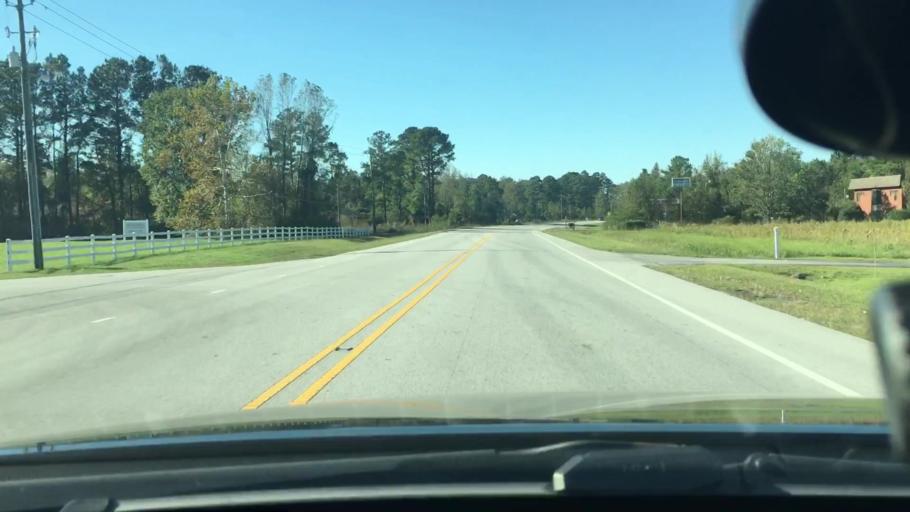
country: US
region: North Carolina
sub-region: Craven County
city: Trent Woods
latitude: 35.1591
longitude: -77.1161
